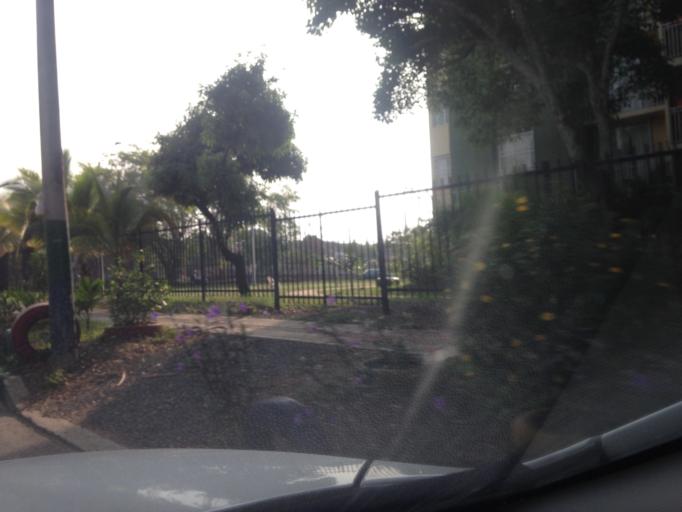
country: CO
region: Valle del Cauca
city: Cali
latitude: 3.4175
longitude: -76.4922
